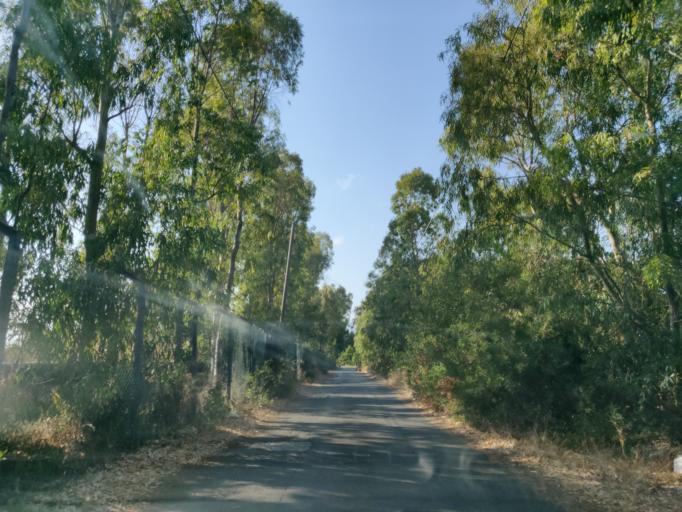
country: IT
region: Latium
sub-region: Citta metropolitana di Roma Capitale
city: Aurelia
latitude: 42.1358
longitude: 11.7611
